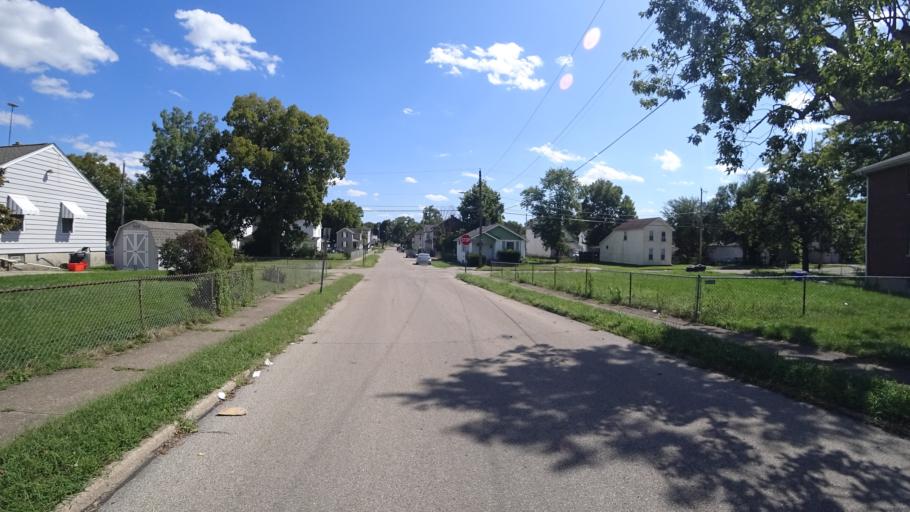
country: US
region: Ohio
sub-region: Butler County
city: Hamilton
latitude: 39.4047
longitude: -84.5503
